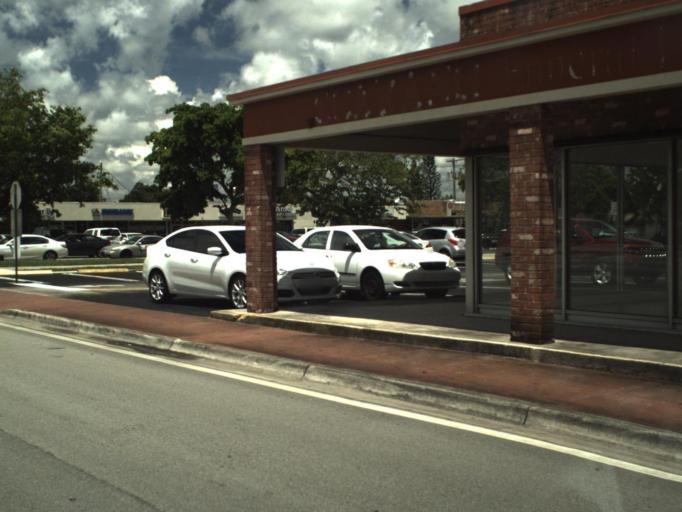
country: US
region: Florida
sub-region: Broward County
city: Carver Ranches
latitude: 26.0106
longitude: -80.1891
